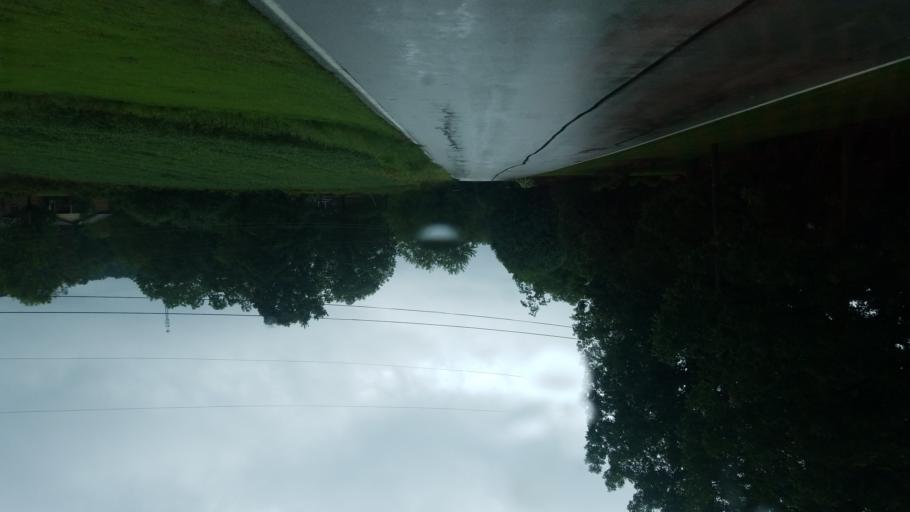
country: US
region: Kentucky
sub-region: Rowan County
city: Morehead
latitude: 38.1774
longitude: -83.4904
